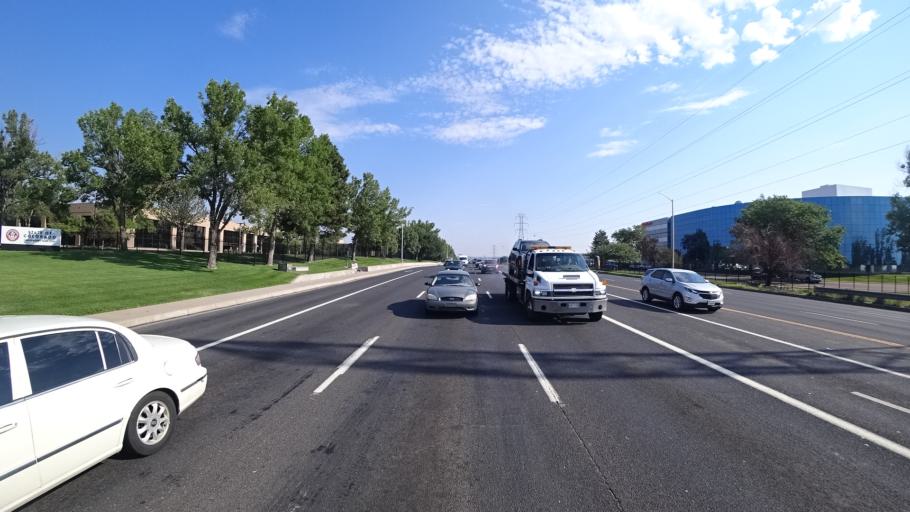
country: US
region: Colorado
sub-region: El Paso County
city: Stratmoor
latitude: 38.8140
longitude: -104.7576
